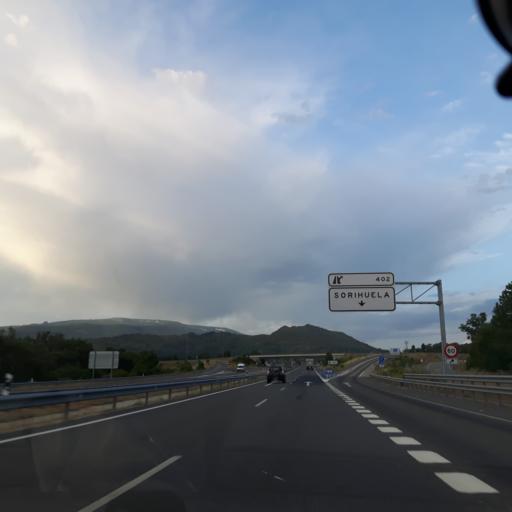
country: ES
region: Castille and Leon
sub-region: Provincia de Salamanca
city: Sorihuela
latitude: 40.4538
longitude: -5.6817
